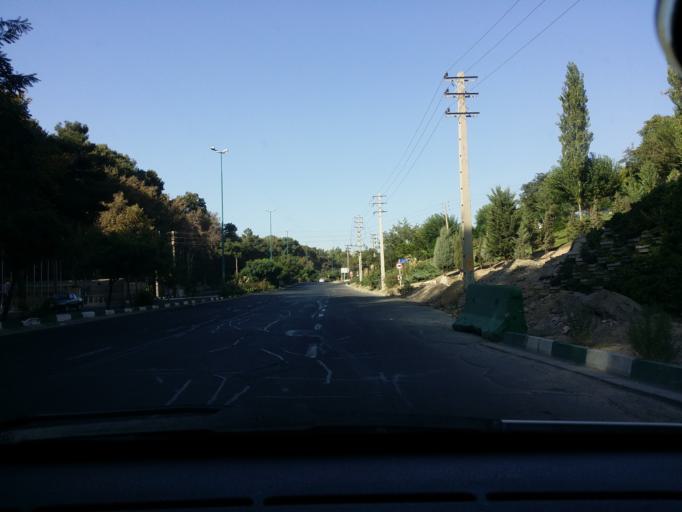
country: IR
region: Alborz
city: Karaj
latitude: 35.8296
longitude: 51.0283
